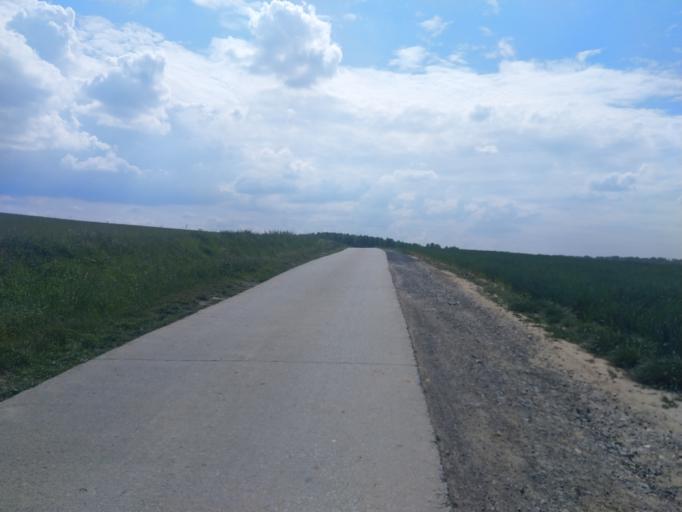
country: BE
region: Wallonia
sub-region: Province du Hainaut
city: Chasse Royale
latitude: 50.4245
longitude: 3.9793
